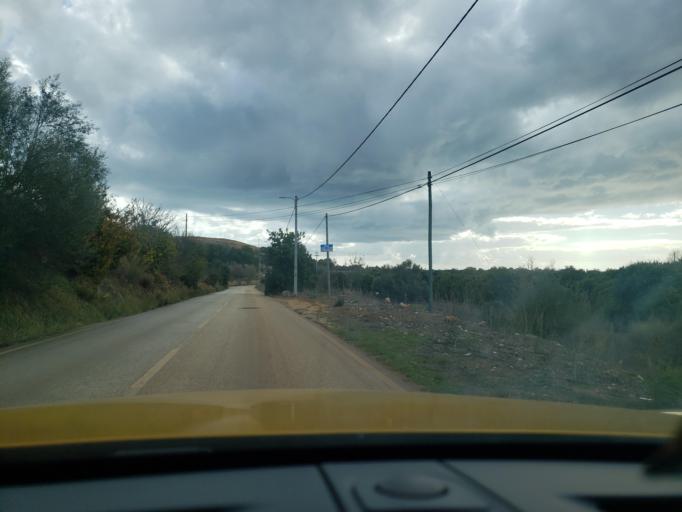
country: PT
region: Faro
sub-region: Portimao
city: Alvor
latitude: 37.1744
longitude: -8.5788
